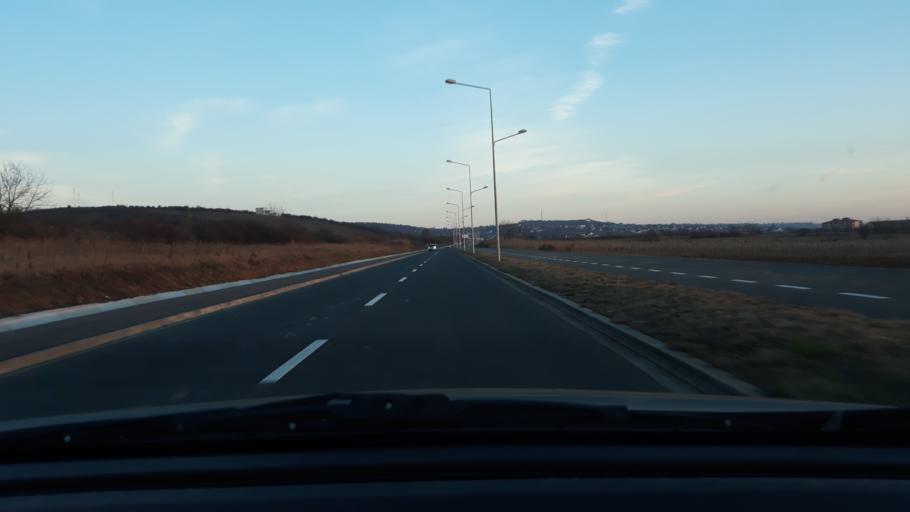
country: RO
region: Bihor
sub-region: Comuna Biharea
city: Oradea
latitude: 47.1015
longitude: 21.9127
